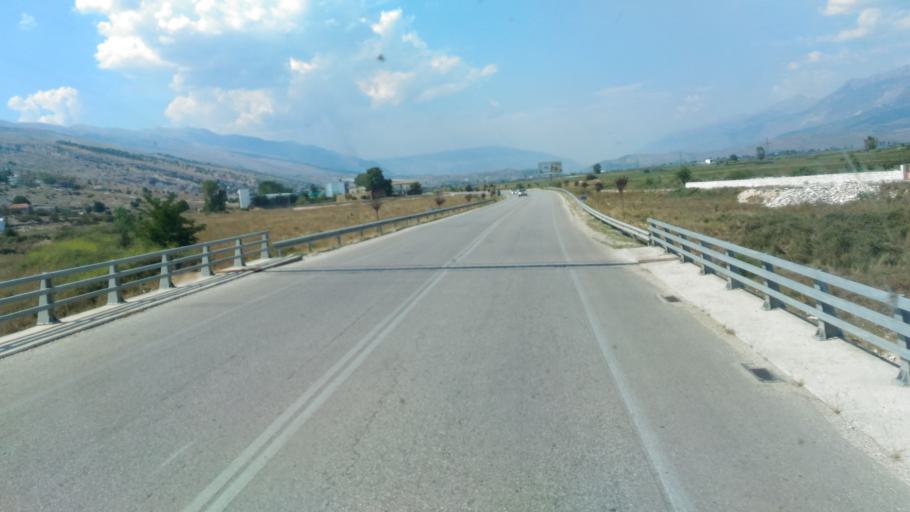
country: AL
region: Gjirokaster
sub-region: Rrethi i Gjirokastres
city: Dervician
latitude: 40.0033
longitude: 20.2109
